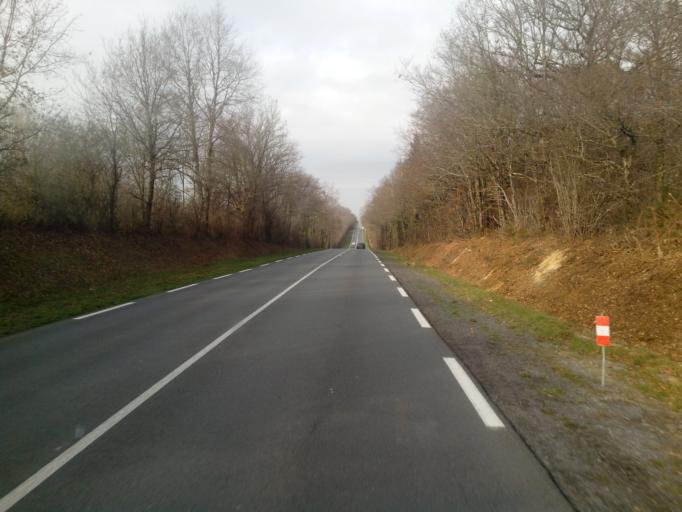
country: FR
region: Limousin
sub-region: Departement de la Haute-Vienne
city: Bussiere-Poitevine
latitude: 46.2731
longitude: 0.8611
